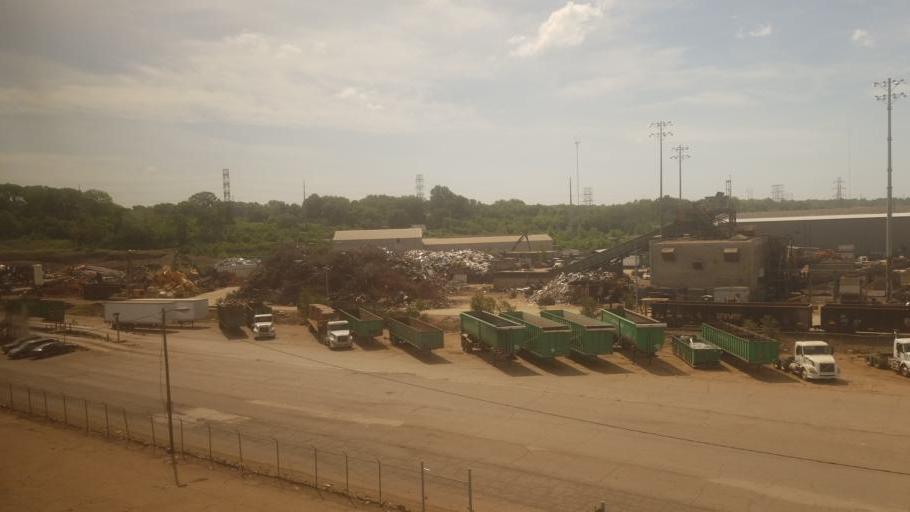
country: US
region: Missouri
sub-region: Jackson County
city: Sugar Creek
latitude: 39.1113
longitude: -94.4942
